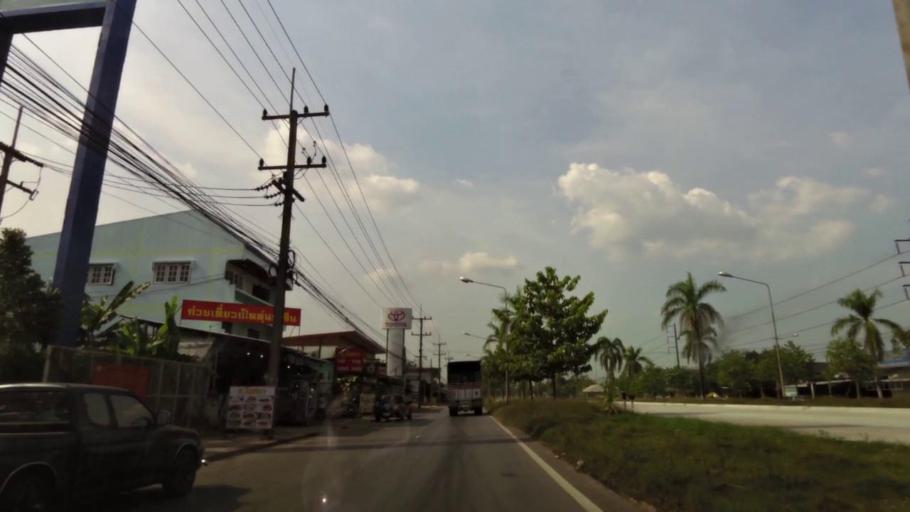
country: TH
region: Rayong
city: Klaeng
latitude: 12.7926
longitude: 101.6456
